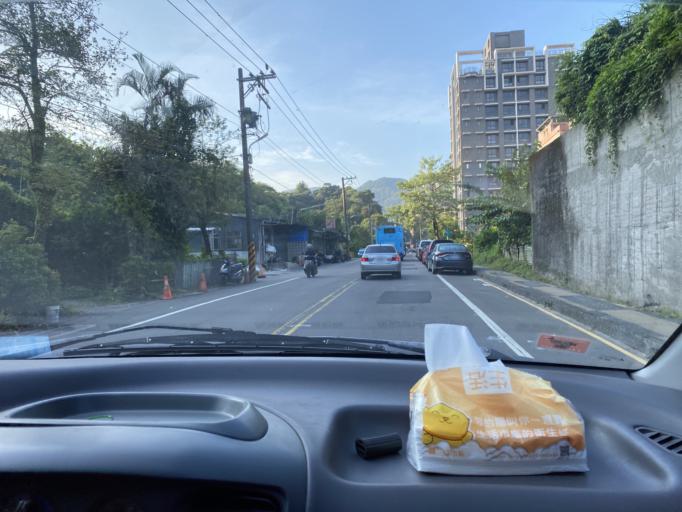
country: TW
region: Taiwan
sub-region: Keelung
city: Keelung
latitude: 25.0976
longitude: 121.7388
